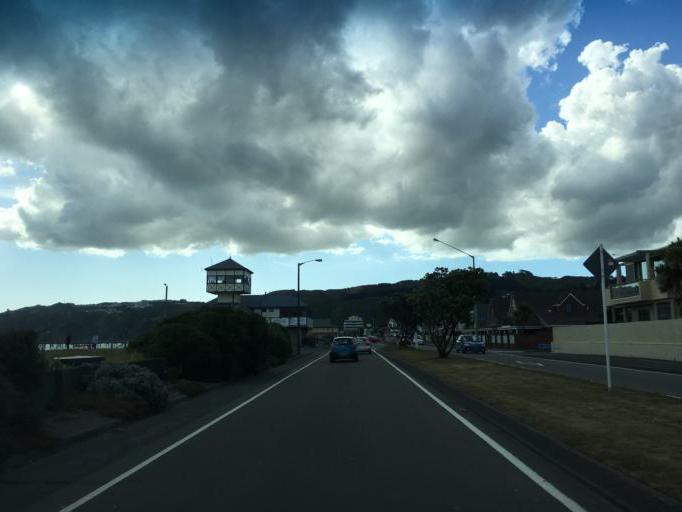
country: NZ
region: Wellington
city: Petone
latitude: -41.2282
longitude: 174.8768
